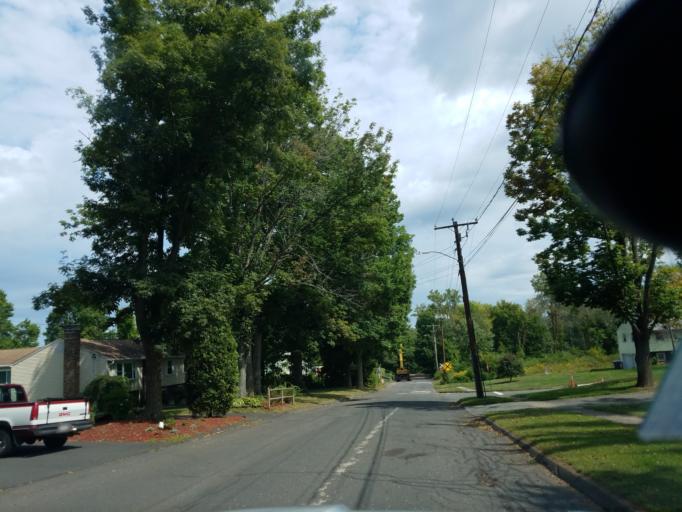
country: US
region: Connecticut
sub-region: Hartford County
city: Wethersfield
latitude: 41.6824
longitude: -72.6471
